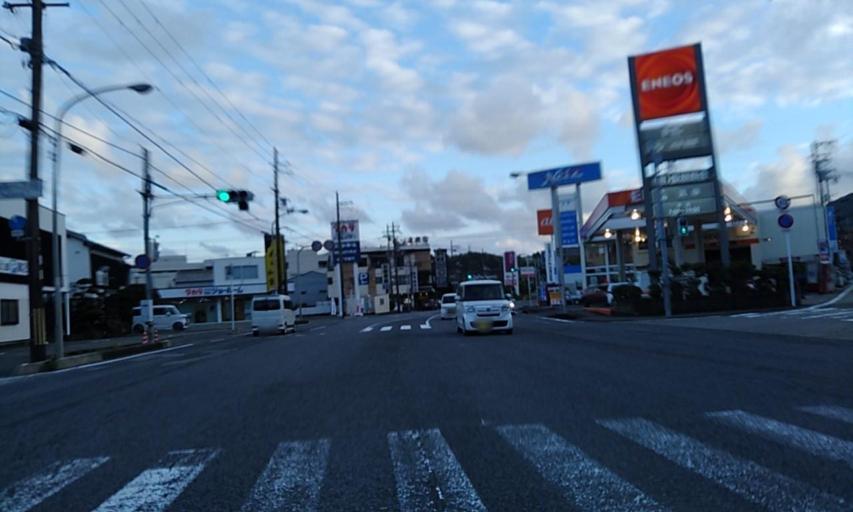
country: JP
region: Wakayama
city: Shingu
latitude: 33.7158
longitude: 135.9881
